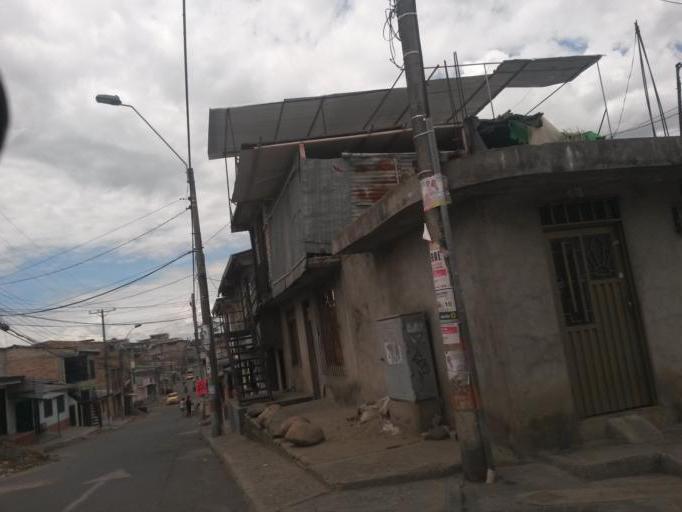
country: CO
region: Cauca
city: Popayan
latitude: 2.4482
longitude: -76.6275
